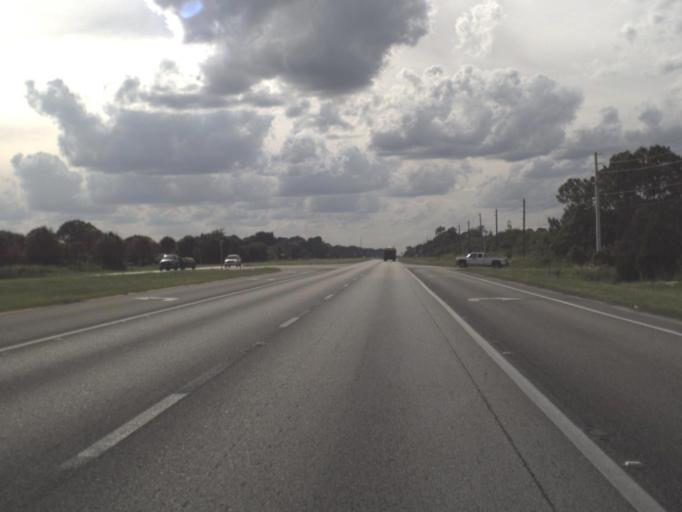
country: US
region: Florida
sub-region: Lee County
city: Alva
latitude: 26.7101
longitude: -81.5168
